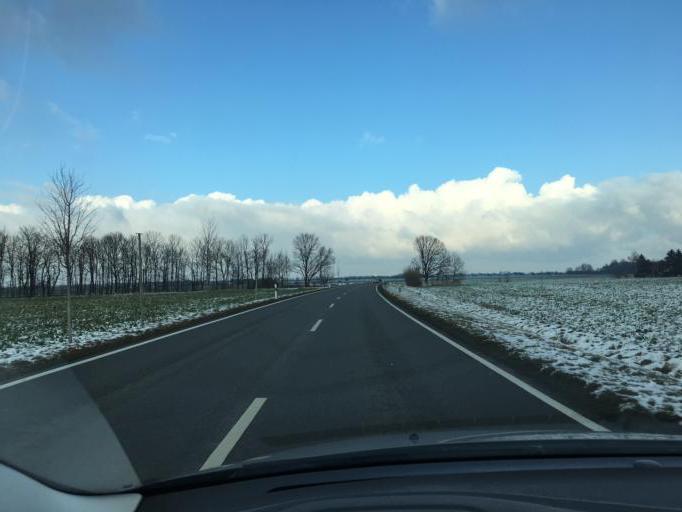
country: DE
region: Saxony
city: Brandis
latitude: 51.3384
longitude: 12.5937
